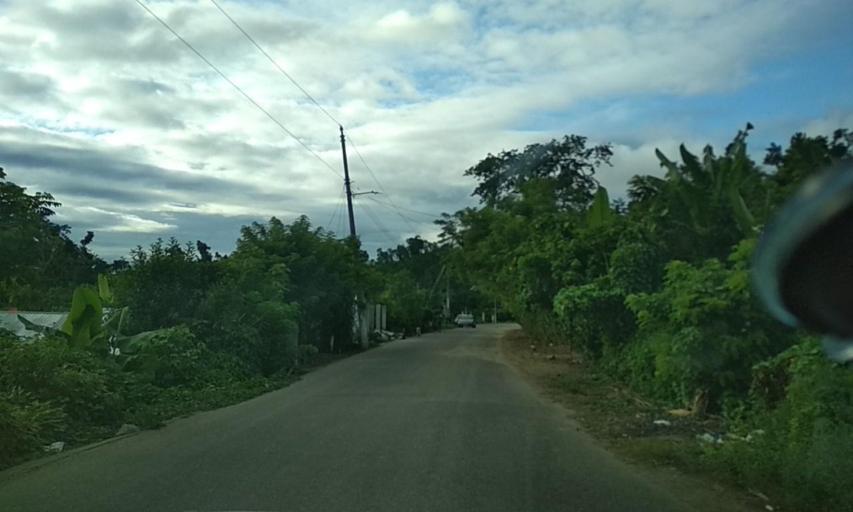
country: MX
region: Veracruz
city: Cazones de Herrera
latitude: 20.6404
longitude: -97.3382
